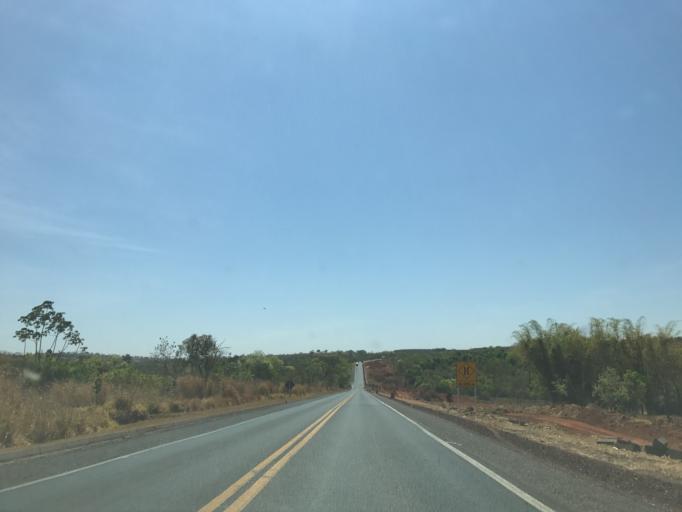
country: BR
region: Minas Gerais
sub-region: Prata
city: Prata
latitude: -19.4172
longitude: -48.8907
